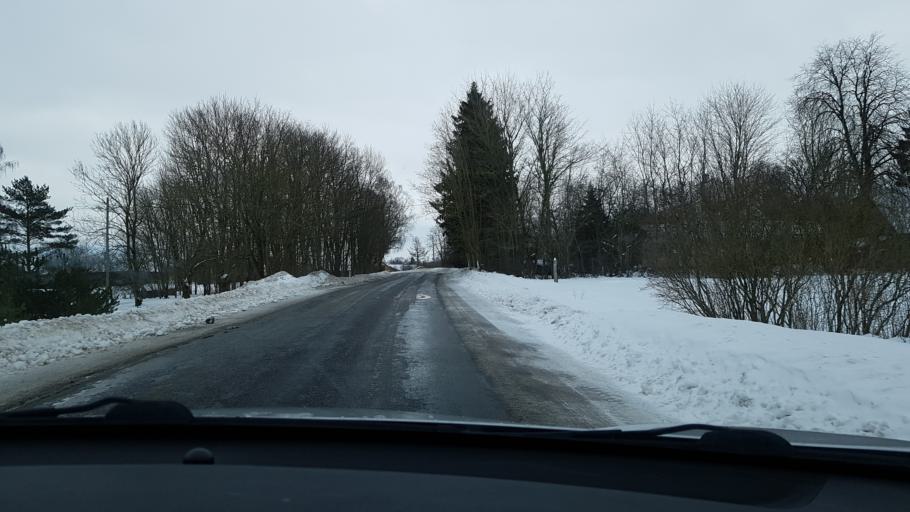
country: EE
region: Jaervamaa
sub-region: Koeru vald
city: Koeru
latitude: 58.9742
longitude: 26.0052
